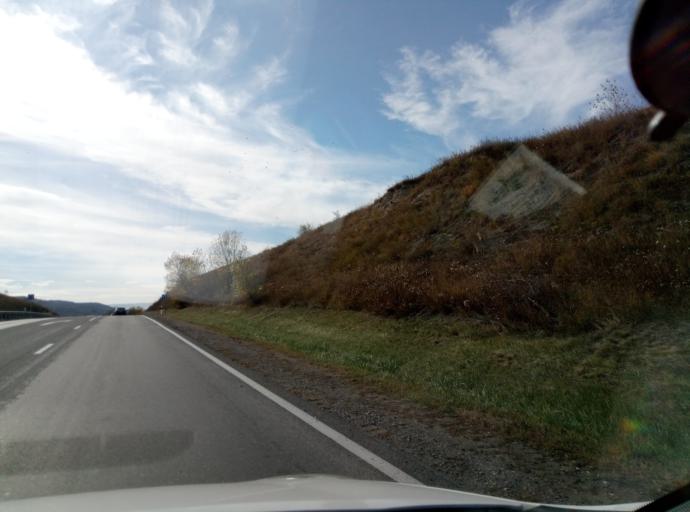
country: RU
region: Stavropol'skiy
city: Yasnaya Polyana
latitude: 43.9772
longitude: 42.7875
